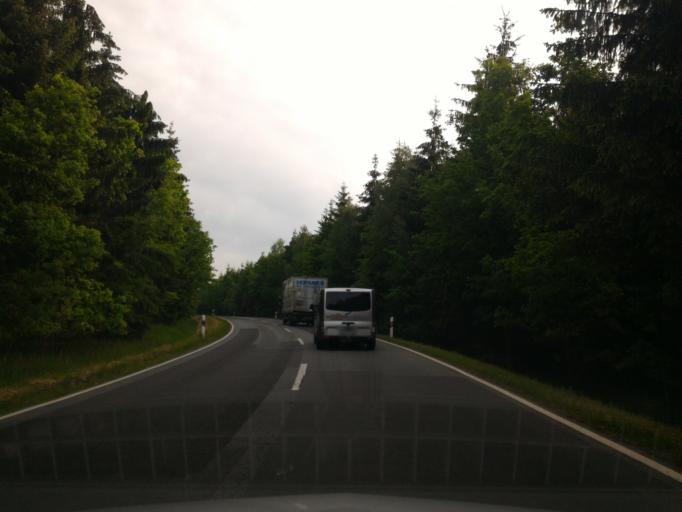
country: DE
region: Saxony
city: Leutersdorf
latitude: 50.9252
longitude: 14.6654
